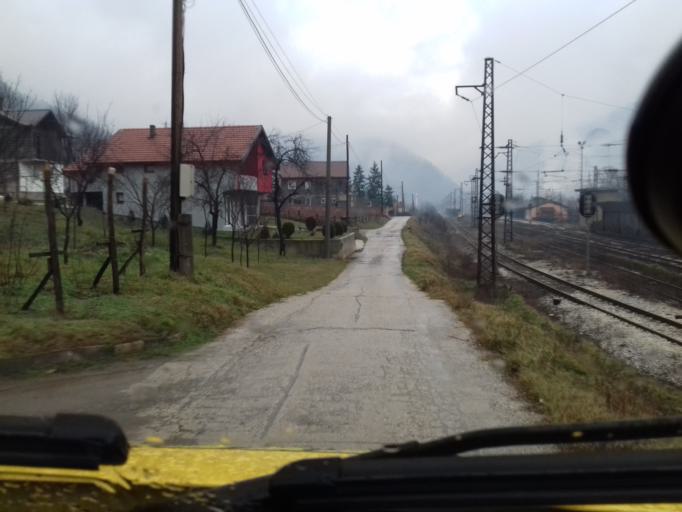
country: BA
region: Federation of Bosnia and Herzegovina
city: Zeljezno Polje
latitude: 44.3242
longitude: 17.9068
